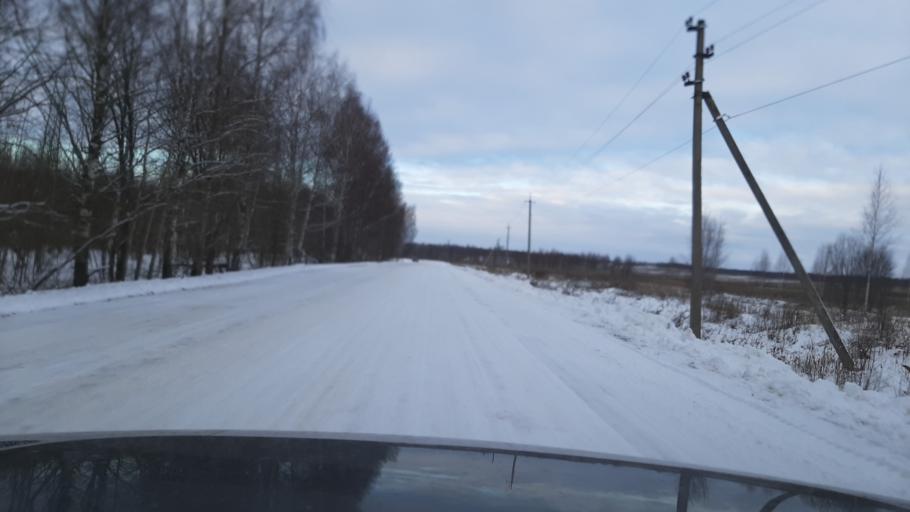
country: RU
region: Kostroma
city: Nerekhta
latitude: 57.4712
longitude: 40.6737
